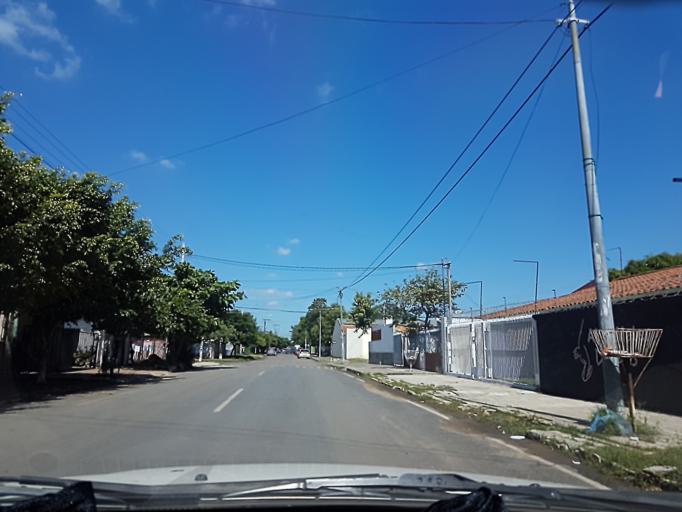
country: PY
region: Central
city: Colonia Mariano Roque Alonso
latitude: -25.2112
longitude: -57.5324
